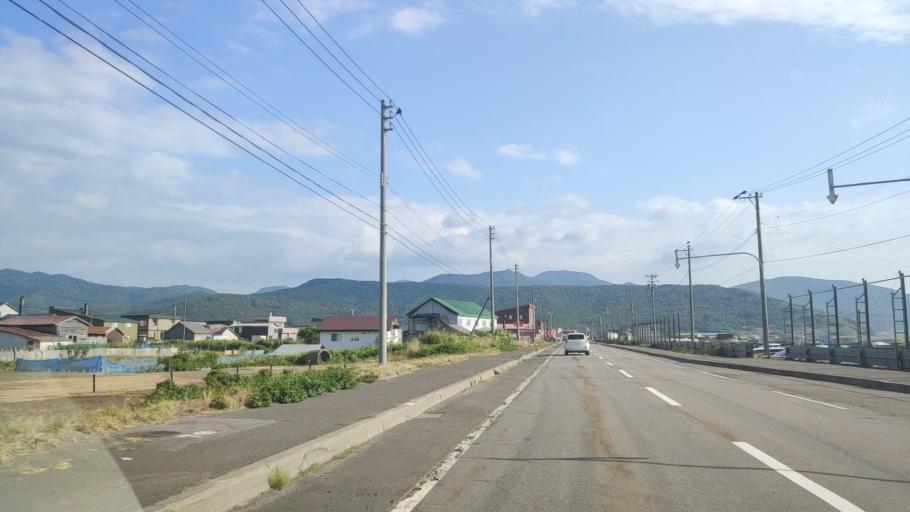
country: JP
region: Hokkaido
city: Ishikari
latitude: 43.5879
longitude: 141.3870
